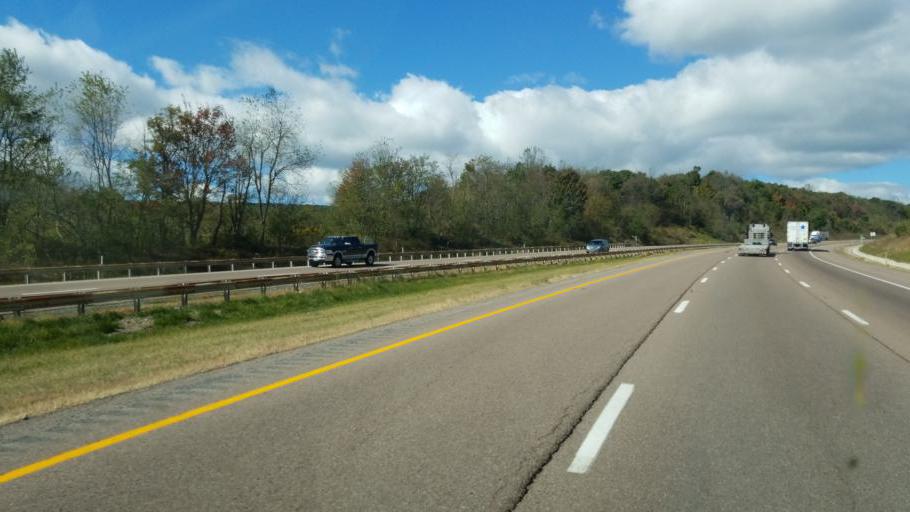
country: US
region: Maryland
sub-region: Allegany County
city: Frostburg
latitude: 39.6472
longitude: -78.9548
